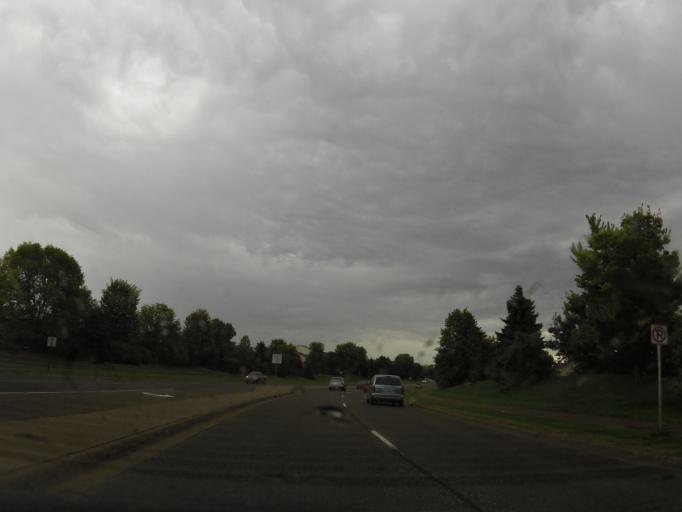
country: US
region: Minnesota
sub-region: Washington County
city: Woodbury
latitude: 44.9376
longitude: -92.9483
